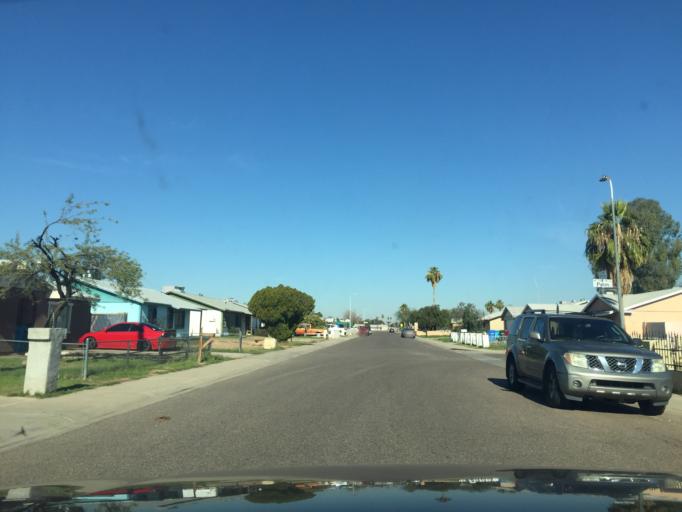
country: US
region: Arizona
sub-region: Maricopa County
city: Tolleson
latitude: 33.4688
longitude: -112.2154
